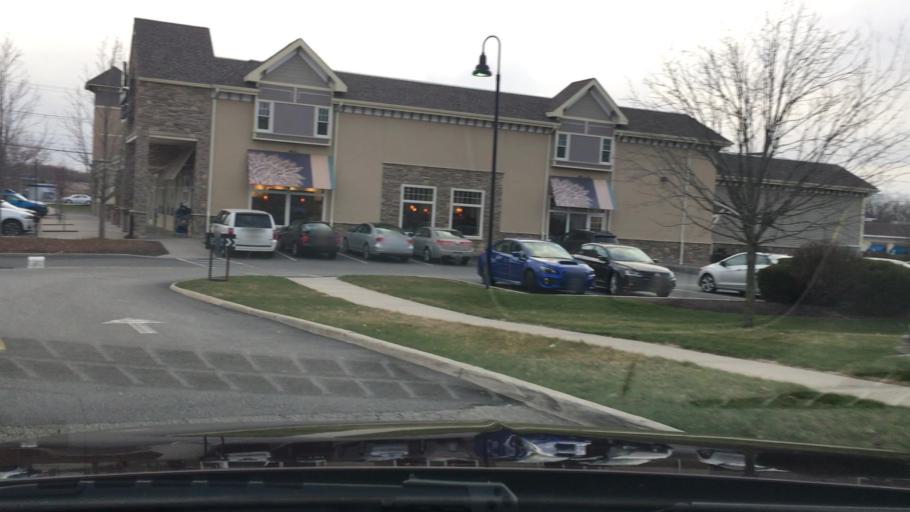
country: US
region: New York
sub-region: Dutchess County
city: Fishkill
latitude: 41.5307
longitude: -73.8923
